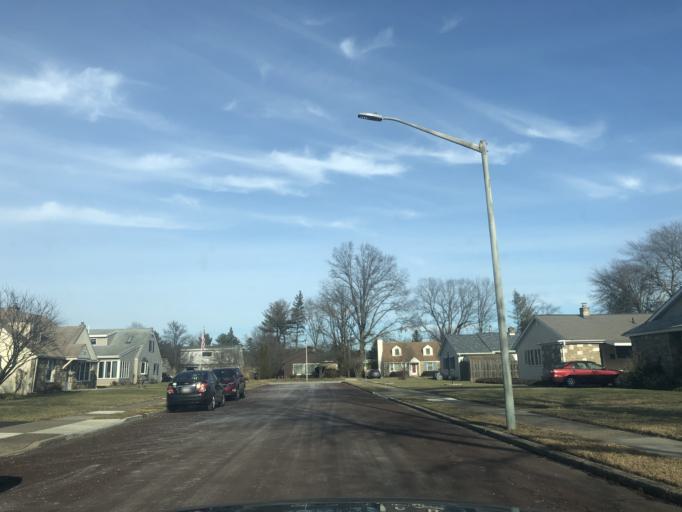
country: US
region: Pennsylvania
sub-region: Montgomery County
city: Flourtown
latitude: 40.1154
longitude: -75.1987
